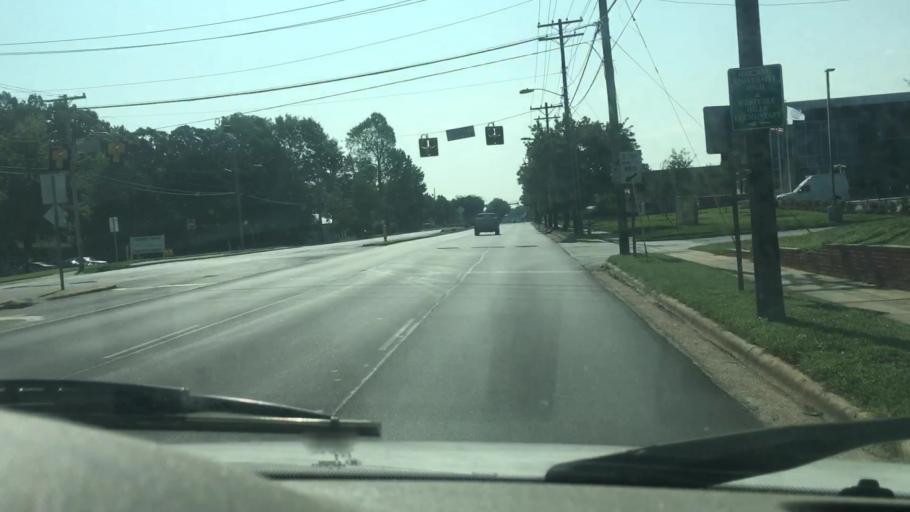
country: US
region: North Carolina
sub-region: Mecklenburg County
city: Charlotte
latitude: 35.2274
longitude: -80.9129
